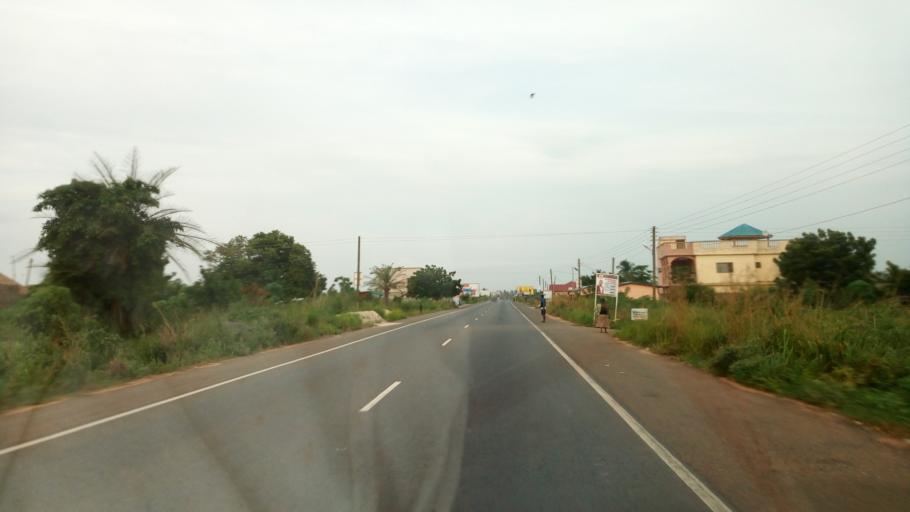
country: TG
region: Maritime
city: Lome
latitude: 6.1119
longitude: 1.1224
